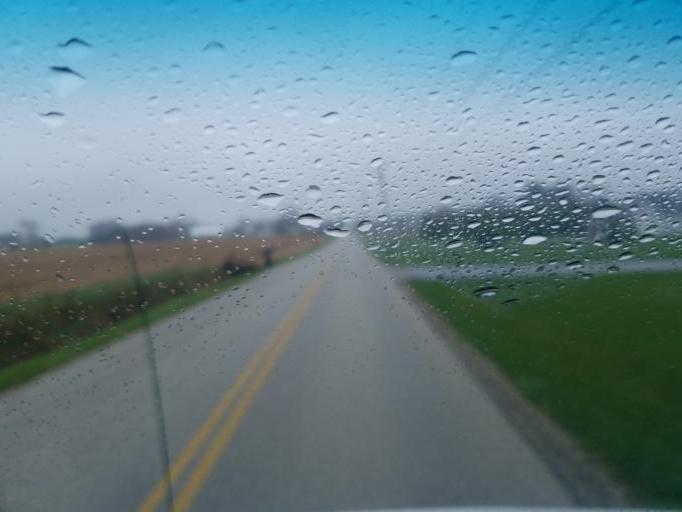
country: US
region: Ohio
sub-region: Wood County
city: North Baltimore
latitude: 41.1495
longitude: -83.6313
